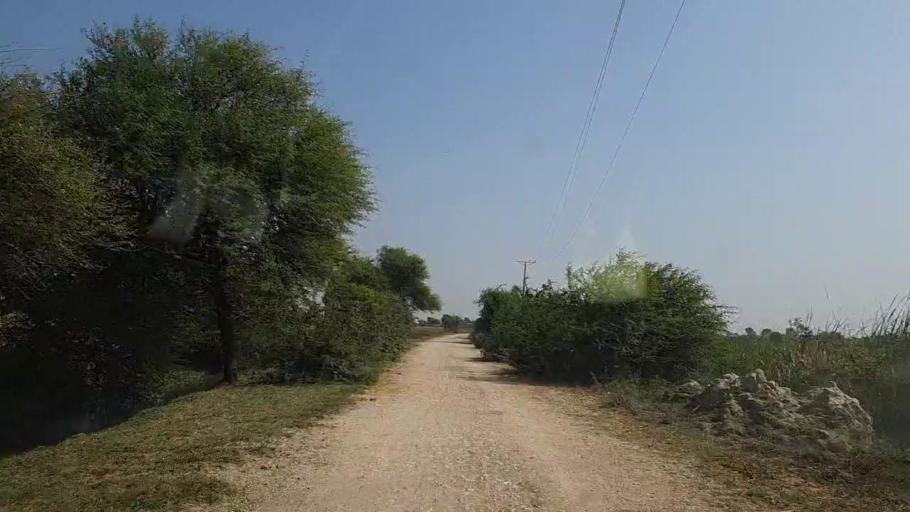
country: PK
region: Sindh
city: Mirpur Sakro
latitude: 24.5269
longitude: 67.8039
